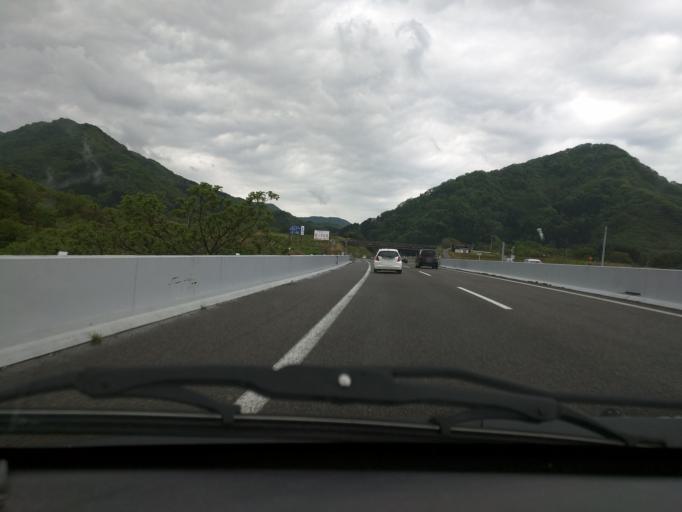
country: JP
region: Niigata
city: Kashiwazaki
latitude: 37.3280
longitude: 138.4604
